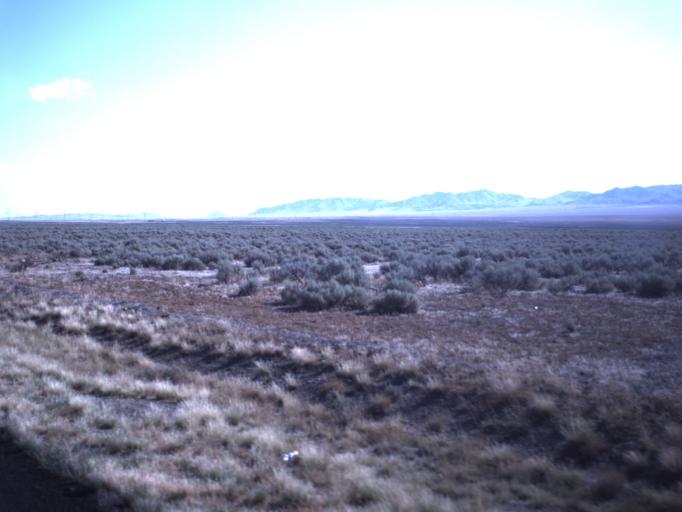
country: US
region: Utah
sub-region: Beaver County
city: Milford
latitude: 38.4237
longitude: -113.0098
